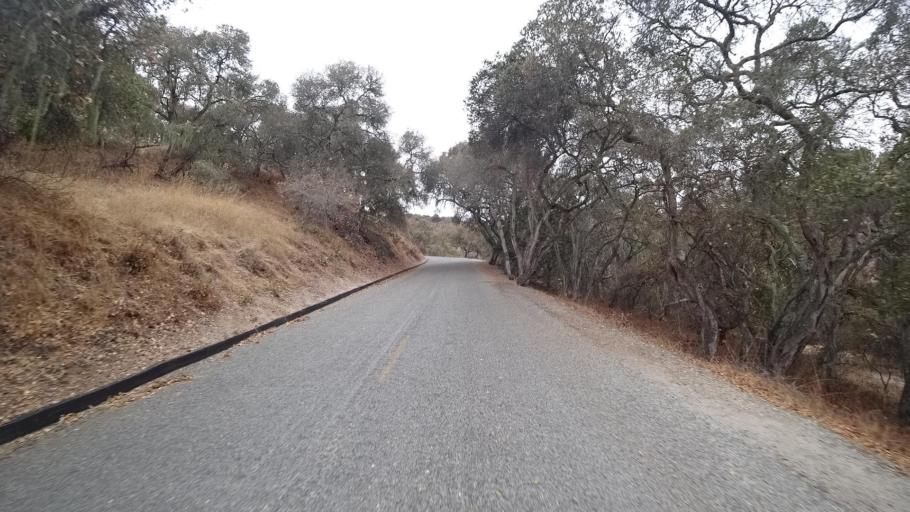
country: US
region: California
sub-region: Monterey County
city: Salinas
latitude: 36.5914
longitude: -121.6939
